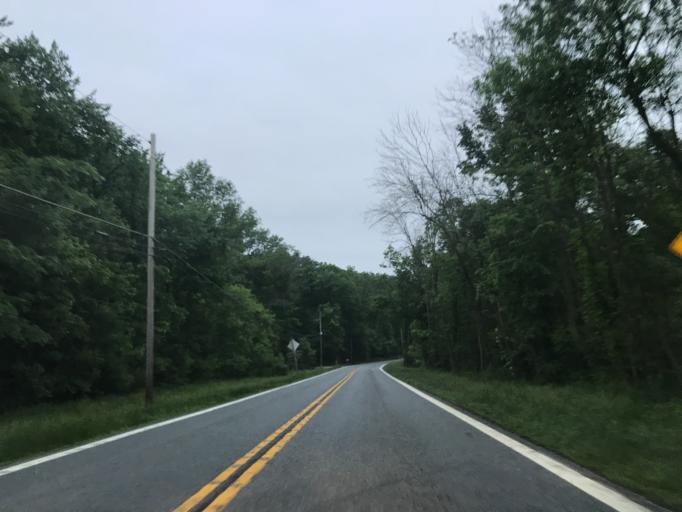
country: US
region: Maryland
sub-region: Frederick County
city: Linganore
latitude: 39.4782
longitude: -77.2438
